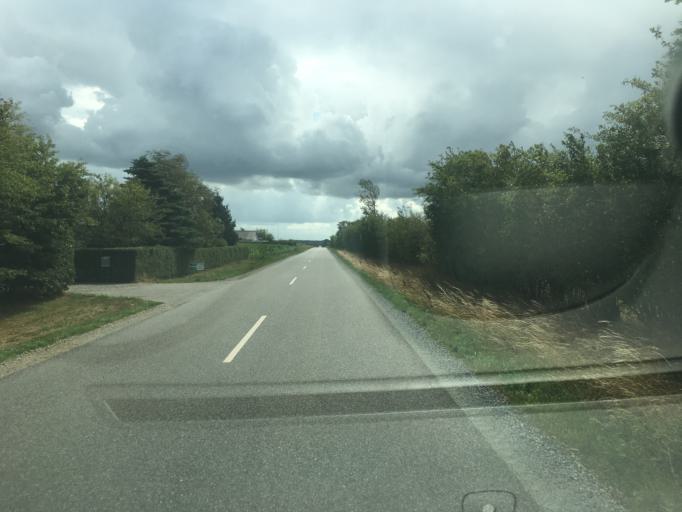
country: DK
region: South Denmark
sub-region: Tonder Kommune
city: Logumkloster
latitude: 55.0438
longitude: 8.9624
